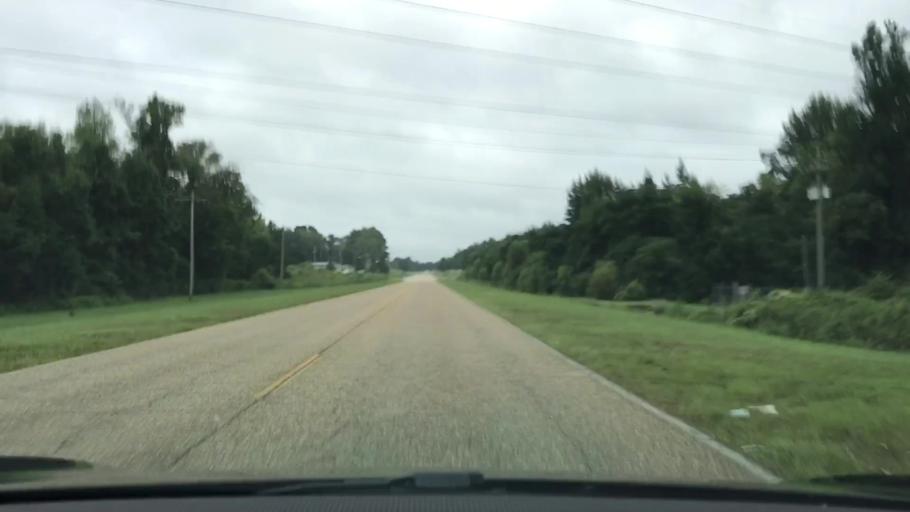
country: US
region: Alabama
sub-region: Coffee County
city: Elba
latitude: 31.4089
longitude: -86.0831
